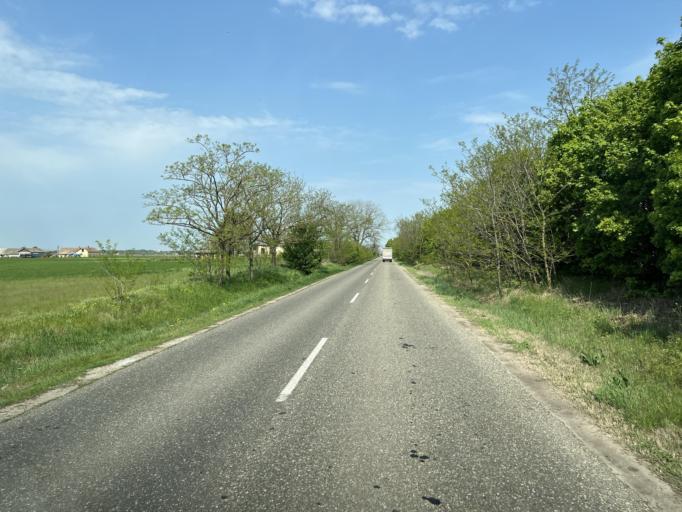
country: HU
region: Pest
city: Tortel
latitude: 47.1127
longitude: 19.9755
